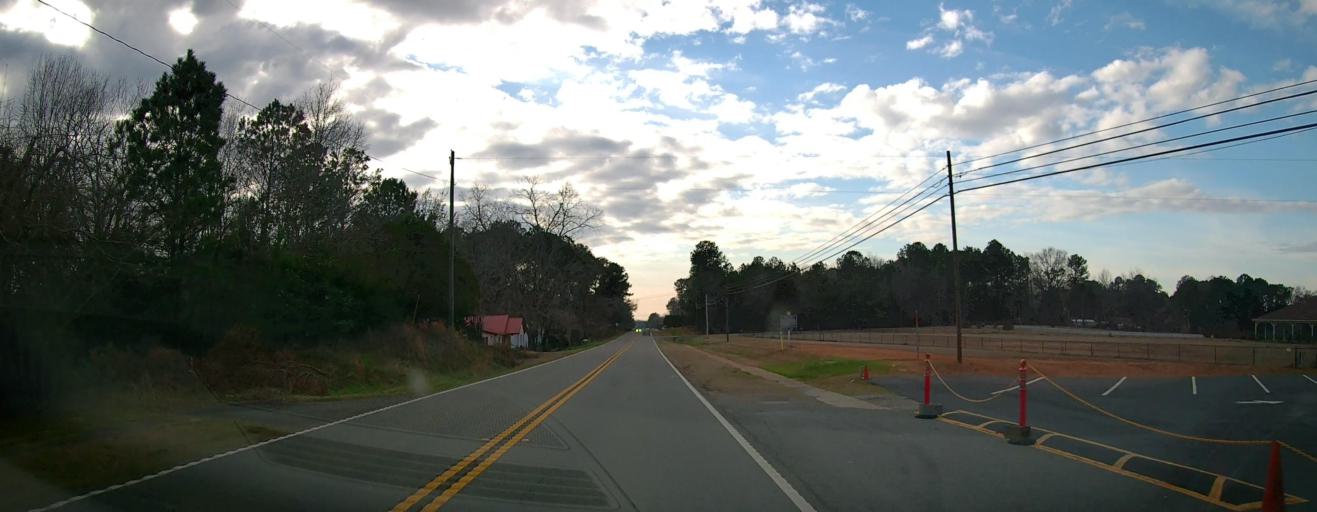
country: US
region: Georgia
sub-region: Harris County
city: Hamilton
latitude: 32.6828
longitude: -84.7484
